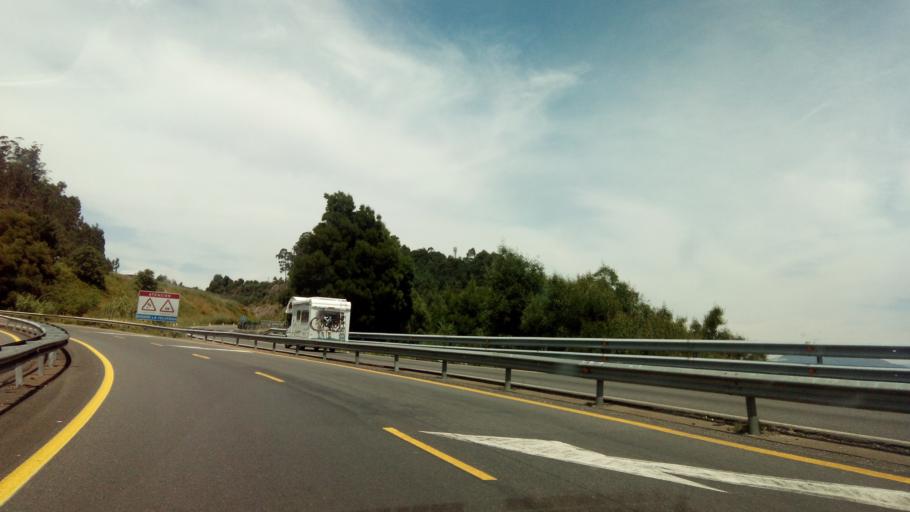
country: ES
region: Galicia
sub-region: Provincia de Pontevedra
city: Redondela
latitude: 42.2941
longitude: -8.6572
